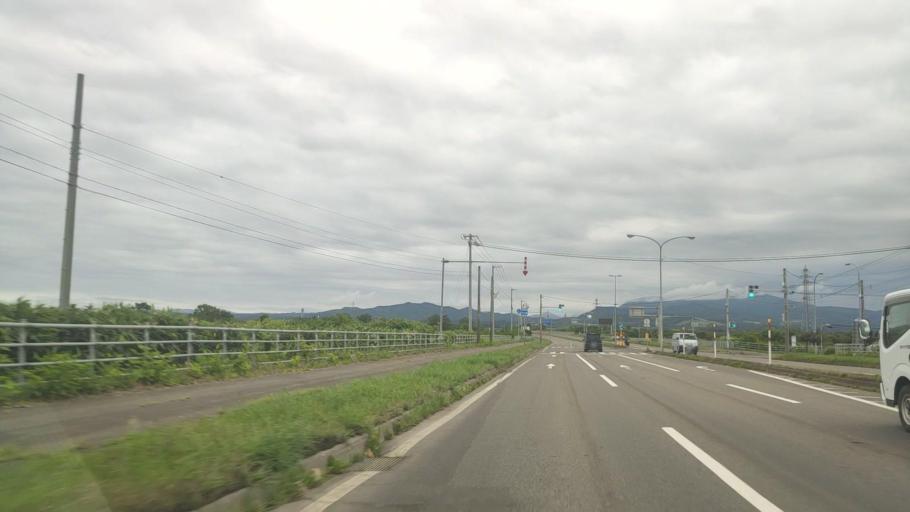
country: JP
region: Hokkaido
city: Nanae
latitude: 42.2679
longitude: 140.2727
